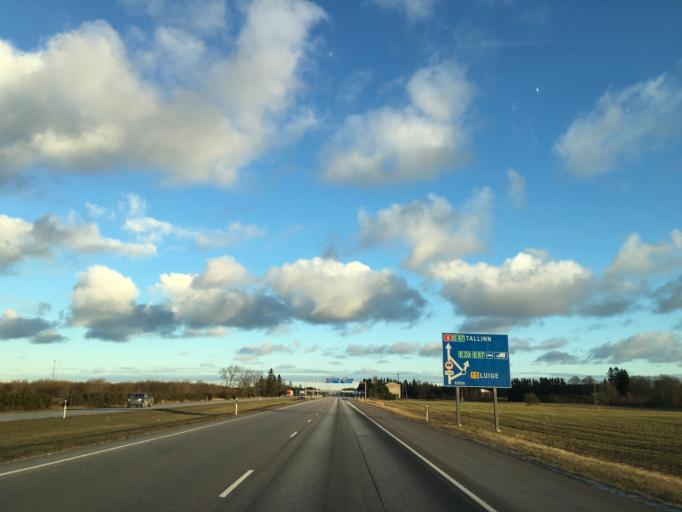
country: EE
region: Harju
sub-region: Saue linn
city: Saue
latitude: 59.3064
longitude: 24.5656
